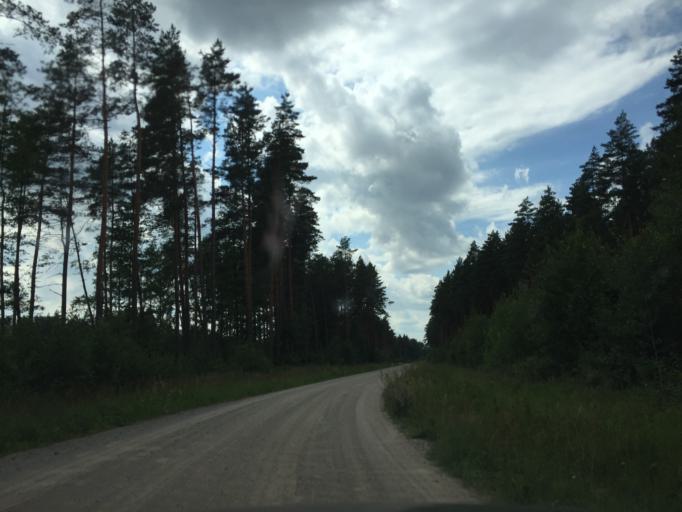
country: LV
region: Jelgava
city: Jelgava
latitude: 56.6256
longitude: 23.6489
